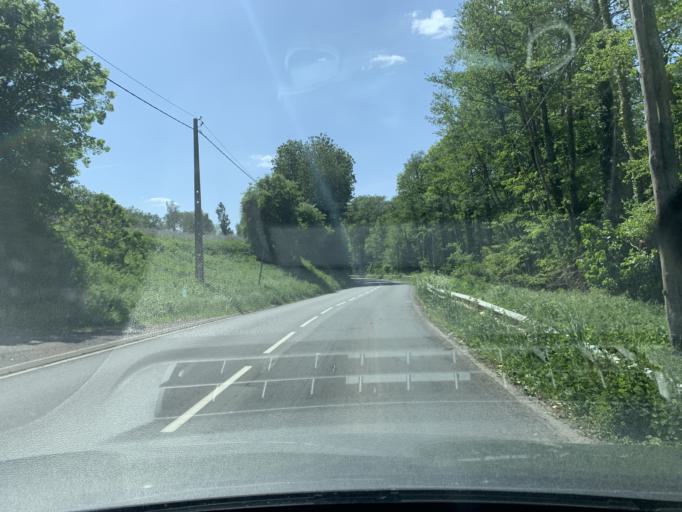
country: FR
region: Nord-Pas-de-Calais
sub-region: Departement du Nord
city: Marcoing
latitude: 50.1263
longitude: 3.1885
